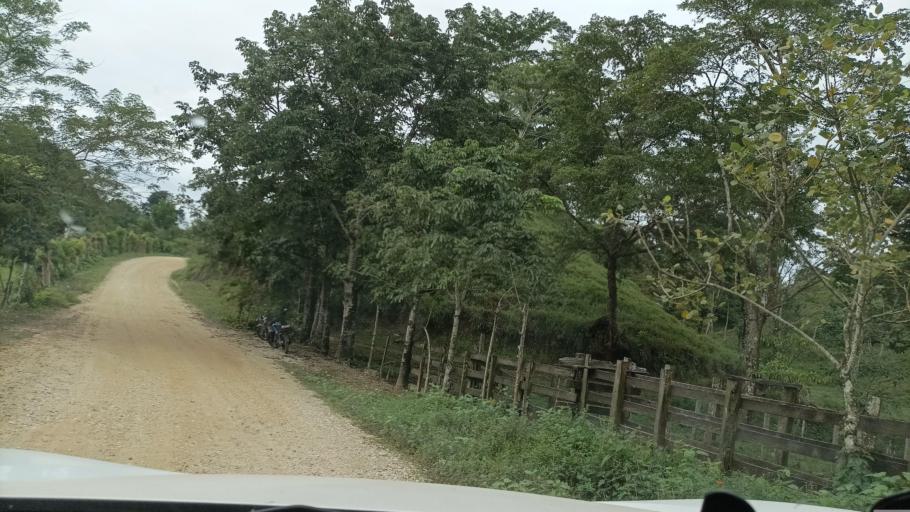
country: MX
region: Veracruz
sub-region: Uxpanapa
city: Poblado 10
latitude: 17.5701
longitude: -94.4233
